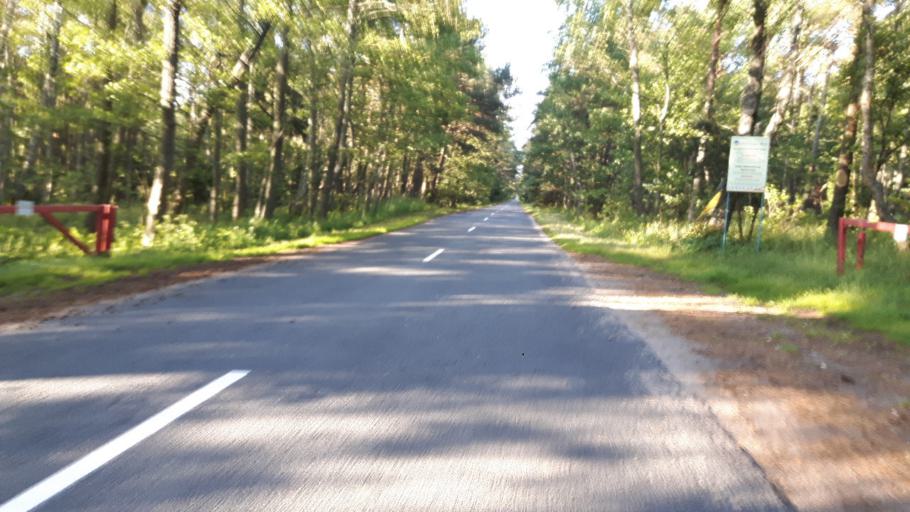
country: LT
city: Nida
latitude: 55.2519
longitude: 20.9284
